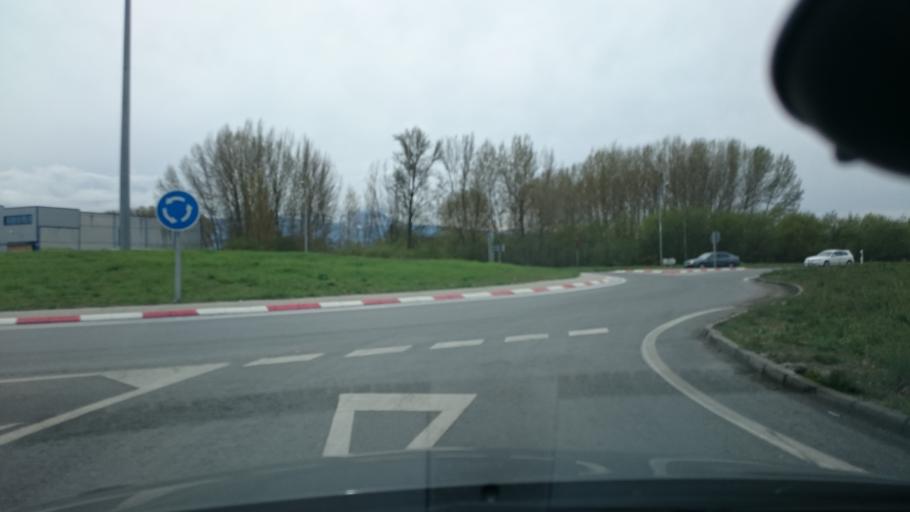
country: ES
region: Castille and Leon
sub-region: Provincia de Leon
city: Camponaraya
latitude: 42.5665
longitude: -6.6586
